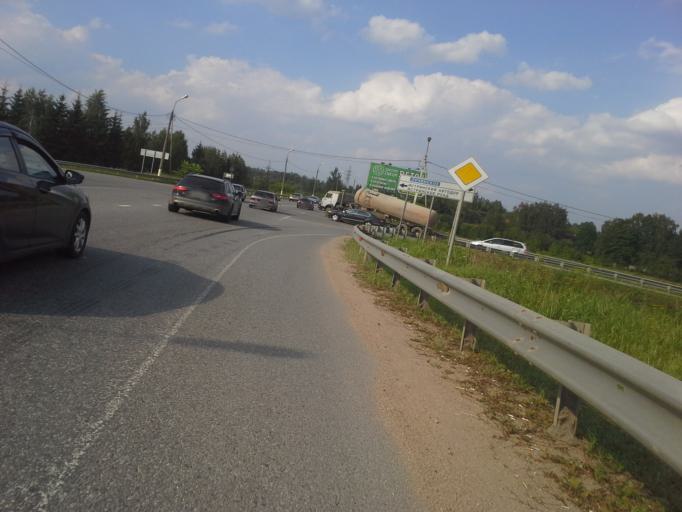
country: RU
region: Moskovskaya
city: Istra
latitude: 55.9093
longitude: 36.8115
